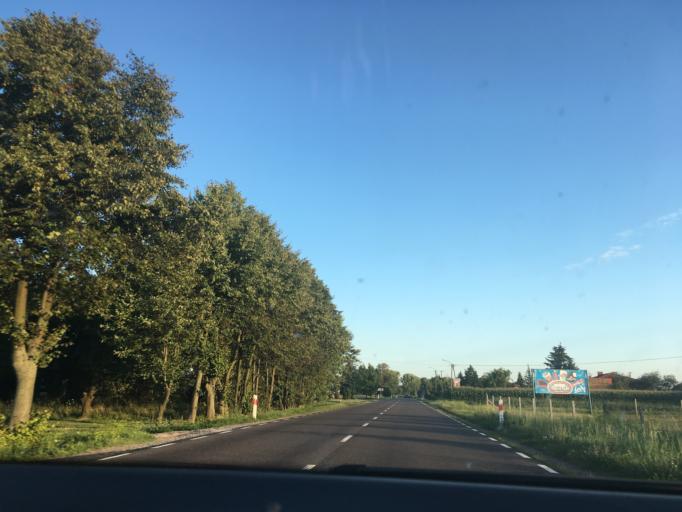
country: PL
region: Lublin Voivodeship
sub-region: Powiat radzynski
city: Radzyn Podlaski
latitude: 51.8523
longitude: 22.6985
